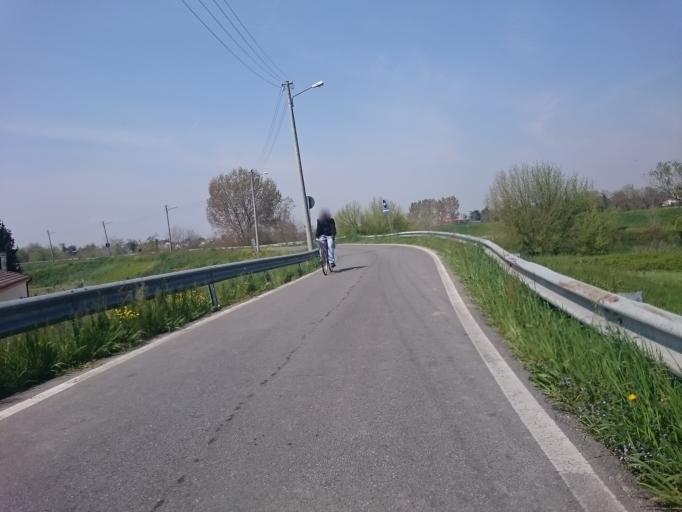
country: IT
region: Veneto
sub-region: Provincia di Padova
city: Tencarola
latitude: 45.3874
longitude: 11.8267
